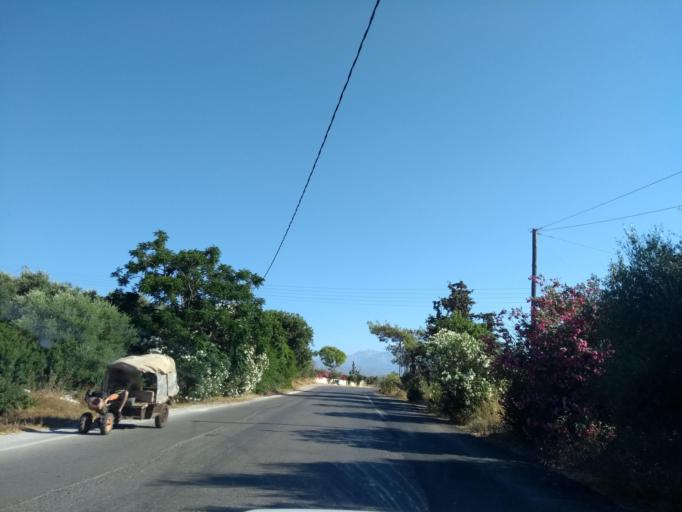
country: GR
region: Crete
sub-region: Nomos Chanias
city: Pithari
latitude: 35.5720
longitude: 24.0916
